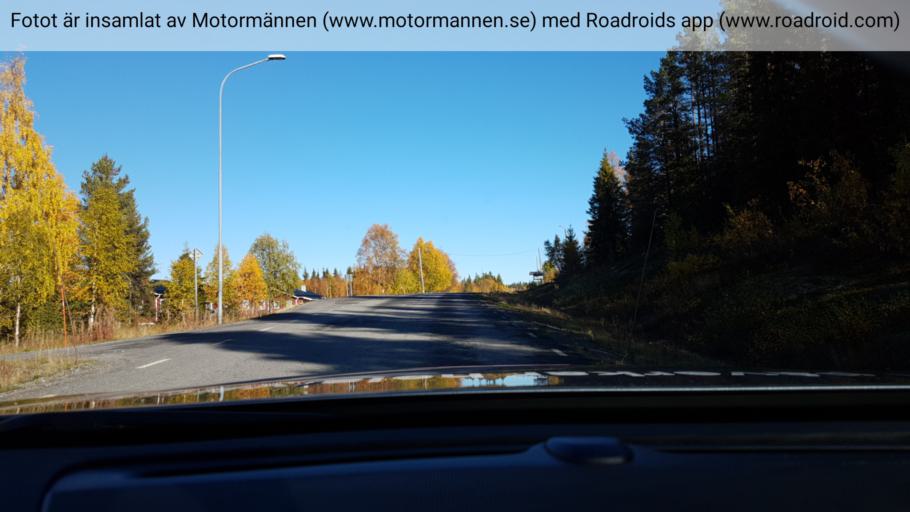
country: SE
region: Norrbotten
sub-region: Gallivare Kommun
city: Gaellivare
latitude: 66.7625
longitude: 21.0269
